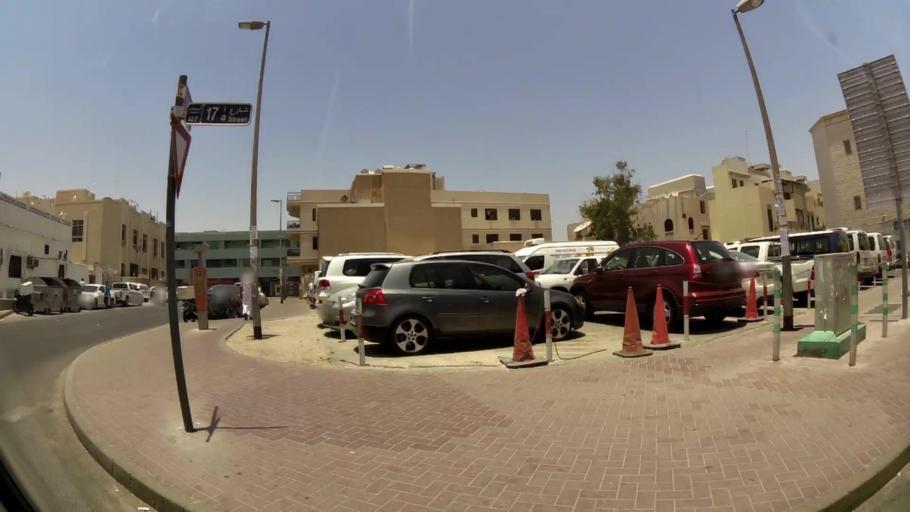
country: AE
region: Ash Shariqah
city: Sharjah
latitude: 25.2765
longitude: 55.3366
